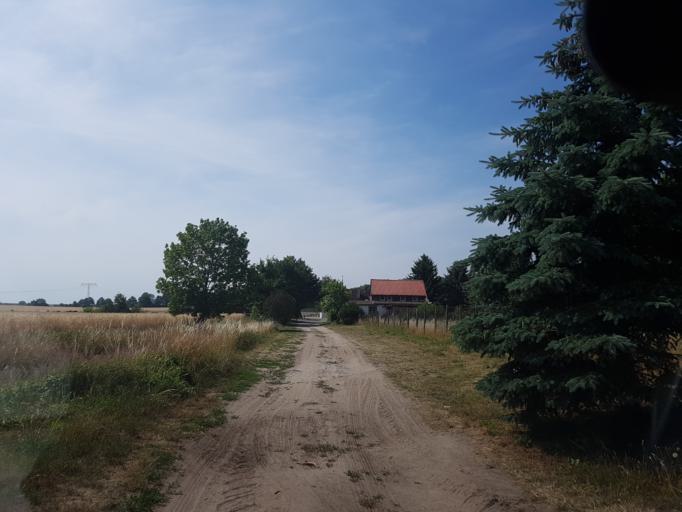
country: DE
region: Brandenburg
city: Teltow
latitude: 52.3759
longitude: 13.2700
